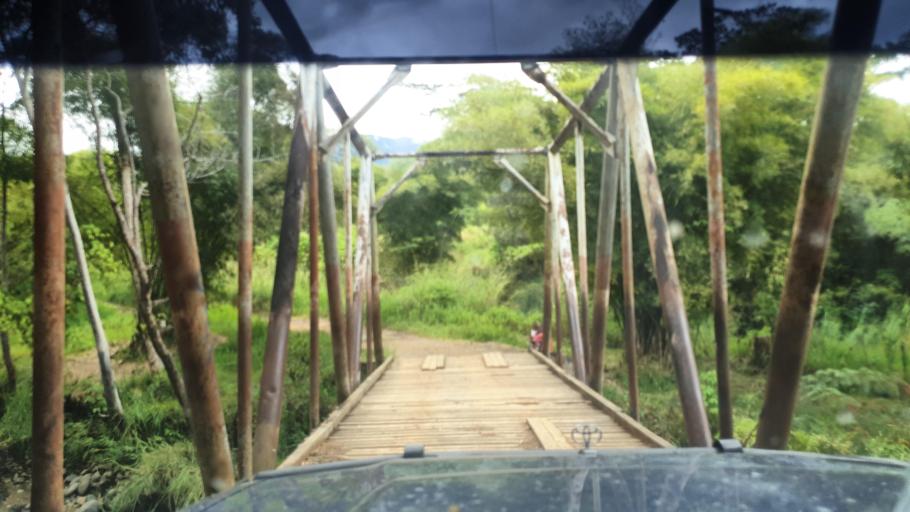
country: PG
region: Jiwaka
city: Minj
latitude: -5.8936
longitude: 144.8163
